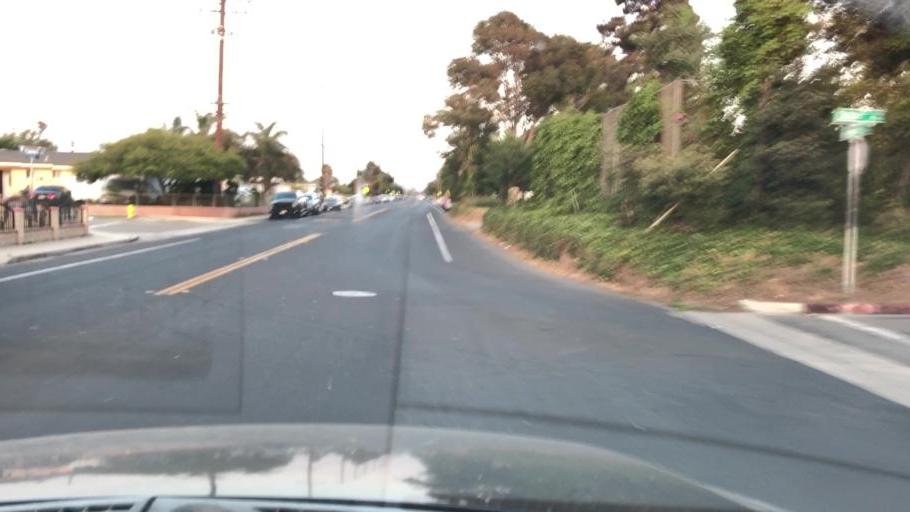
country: US
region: California
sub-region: Ventura County
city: Channel Islands Beach
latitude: 34.1812
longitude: -119.2062
